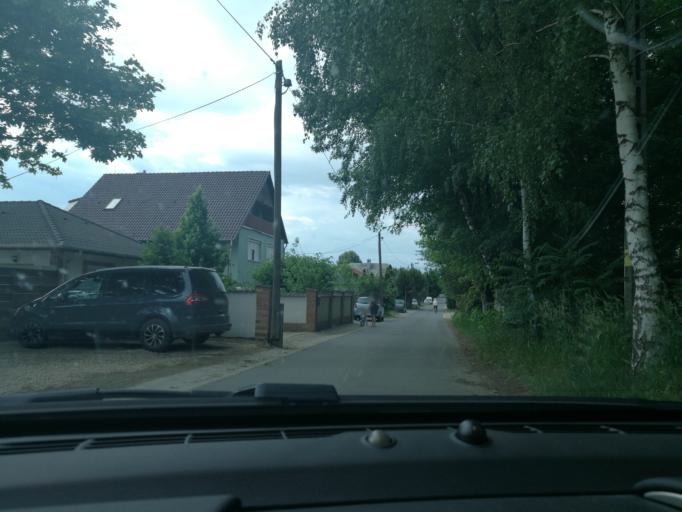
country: HU
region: Szabolcs-Szatmar-Bereg
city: Nyirpazony
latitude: 47.9463
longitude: 21.7743
